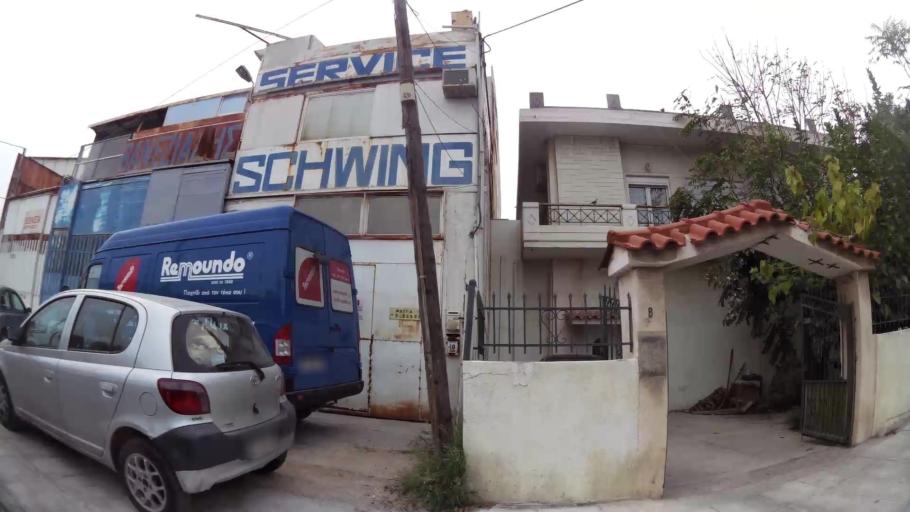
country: GR
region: Attica
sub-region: Nomarchia Athinas
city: Tavros
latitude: 37.9711
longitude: 23.6890
